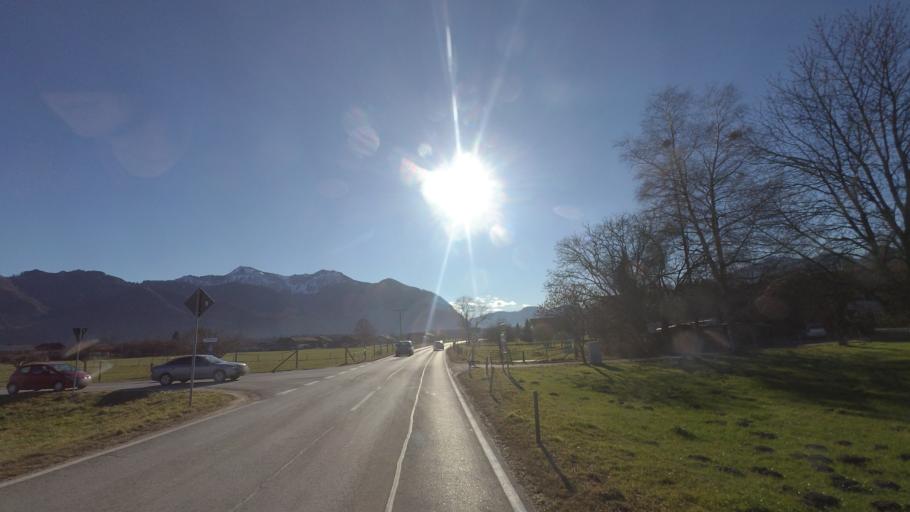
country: DE
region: Bavaria
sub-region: Upper Bavaria
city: Ubersee
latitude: 47.8064
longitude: 12.4820
